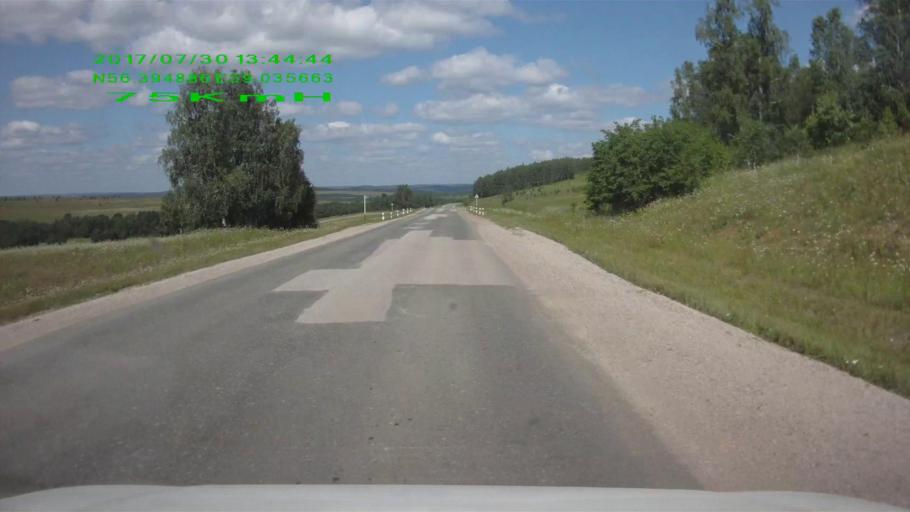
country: RU
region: Sverdlovsk
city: Mikhaylovsk
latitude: 56.3952
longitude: 59.0357
